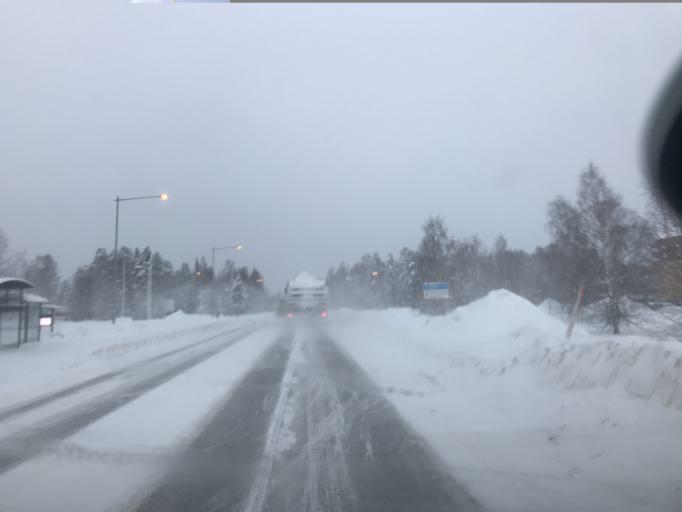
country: SE
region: Norrbotten
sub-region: Lulea Kommun
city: Lulea
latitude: 65.6174
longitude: 22.1311
